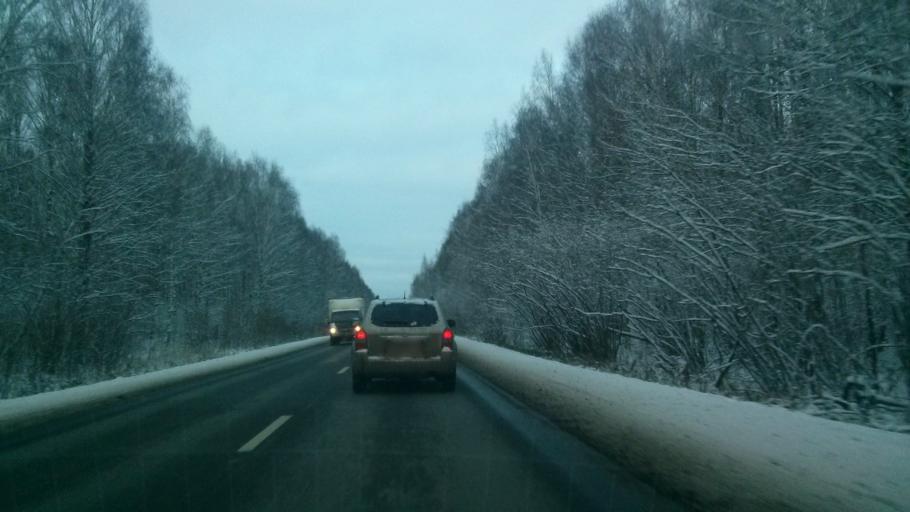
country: RU
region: Nizjnij Novgorod
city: Vorsma
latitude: 56.0161
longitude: 43.3465
